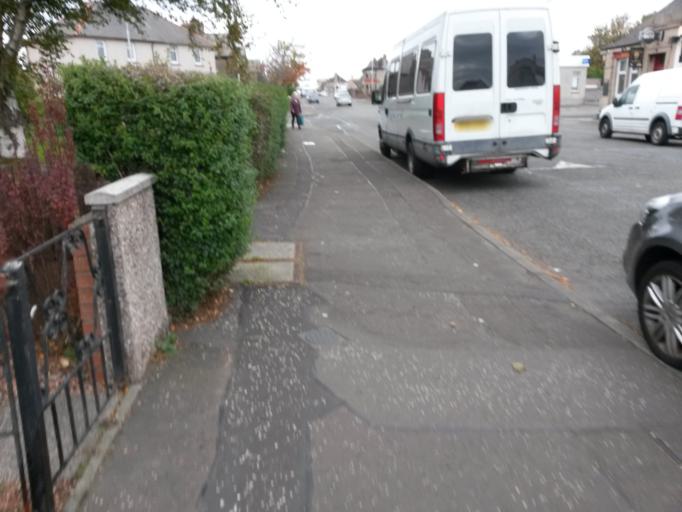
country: GB
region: Scotland
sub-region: Fife
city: Buckhaven
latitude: 56.1749
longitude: -3.0308
